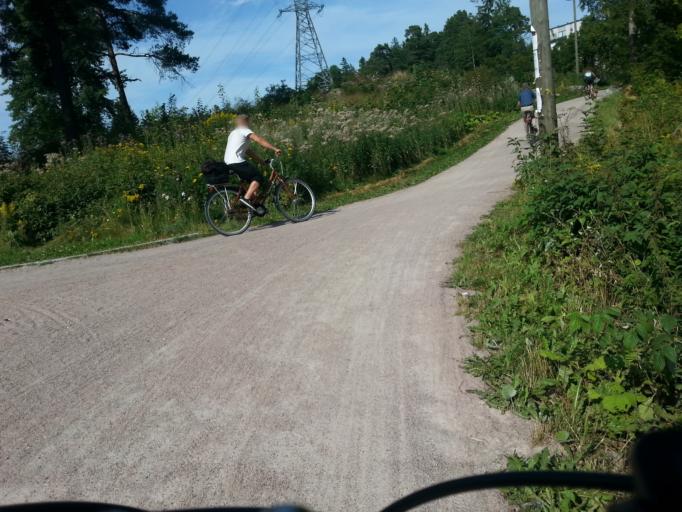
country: FI
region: Uusimaa
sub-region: Helsinki
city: Helsinki
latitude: 60.2245
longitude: 24.9843
